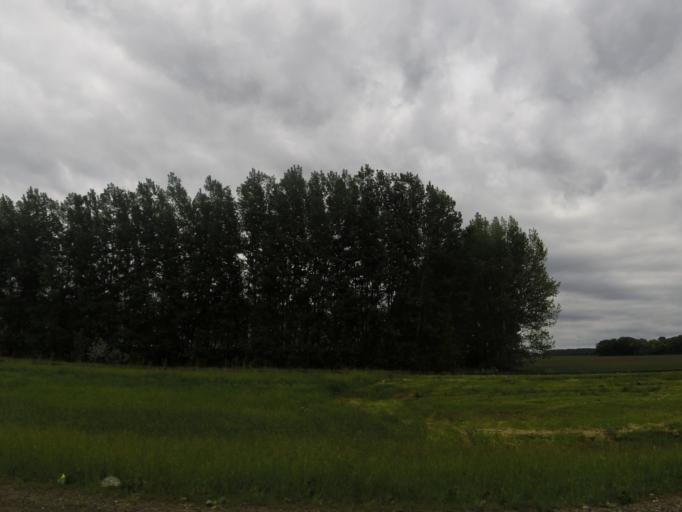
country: US
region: North Dakota
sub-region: Walsh County
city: Grafton
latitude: 48.5938
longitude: -97.4478
